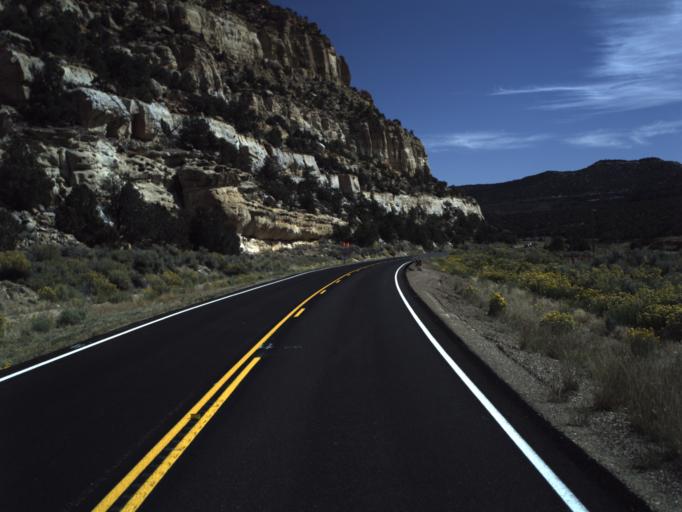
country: US
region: Utah
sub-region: Wayne County
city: Loa
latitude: 37.7380
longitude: -111.7430
